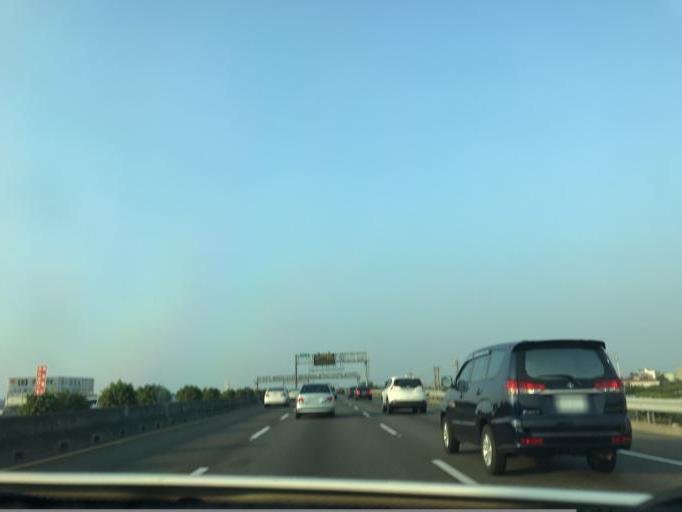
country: TW
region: Taiwan
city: Xinying
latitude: 23.1948
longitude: 120.2364
